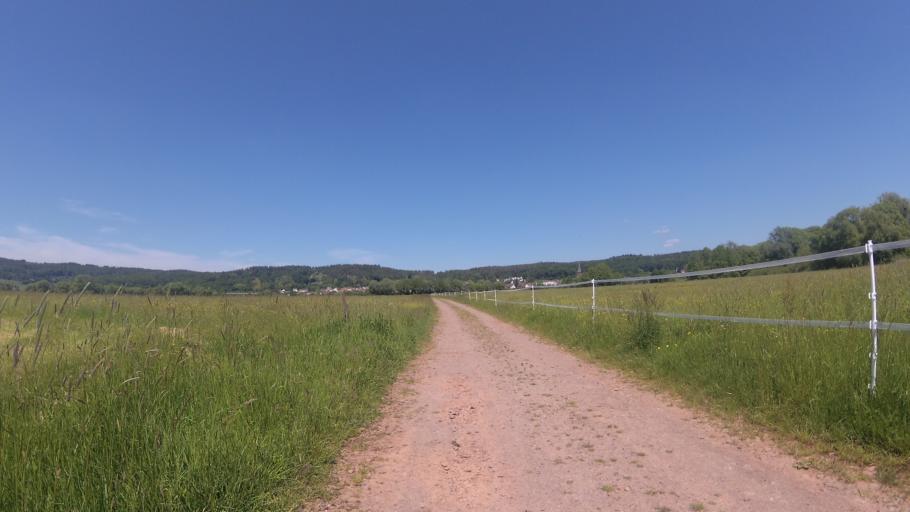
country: DE
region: Saarland
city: Mettlach
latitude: 49.4684
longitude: 6.5997
